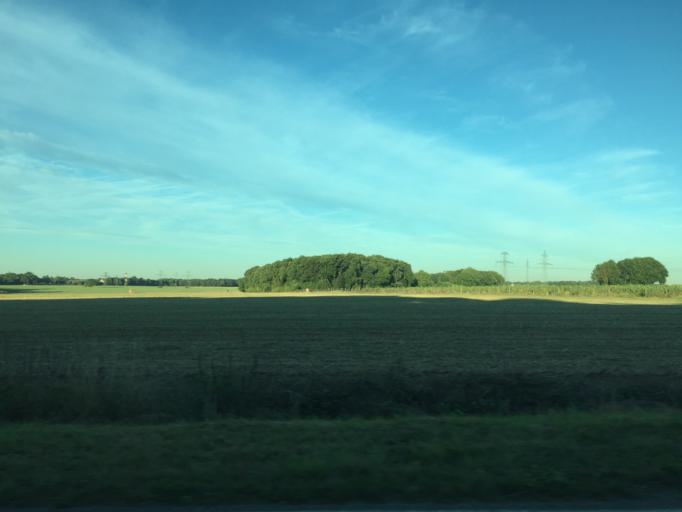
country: FR
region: Ile-de-France
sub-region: Departement des Yvelines
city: Jouy-en-Josas
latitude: 48.7477
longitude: 2.1654
